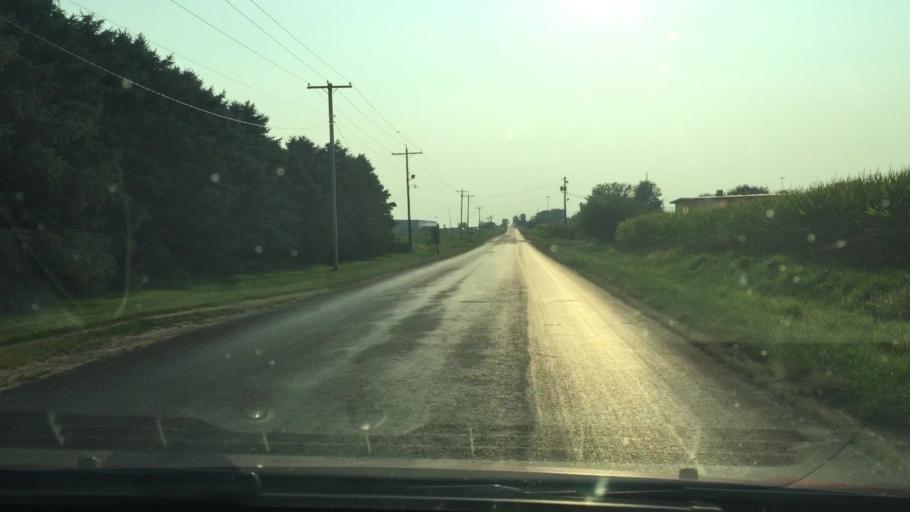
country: US
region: Illinois
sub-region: Bureau County
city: Ladd
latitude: 41.3643
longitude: -89.2105
